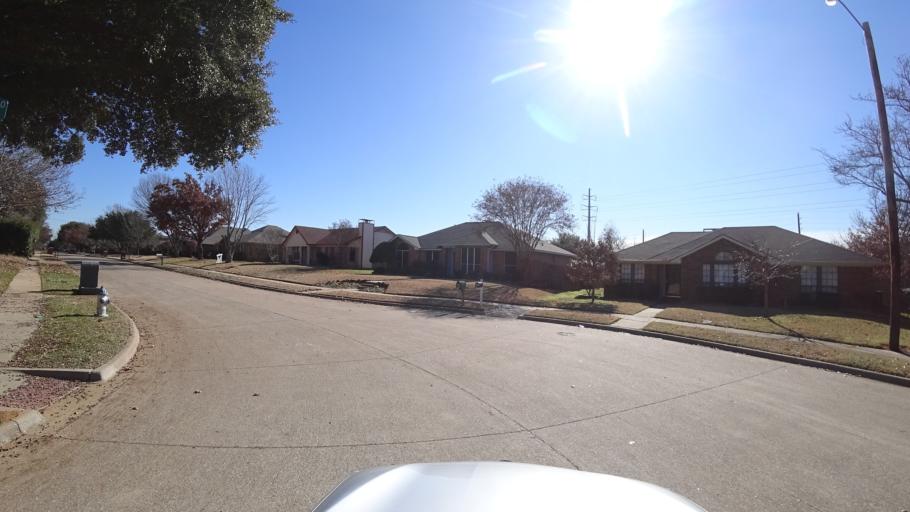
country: US
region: Texas
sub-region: Denton County
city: Lewisville
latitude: 33.0205
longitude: -97.0078
